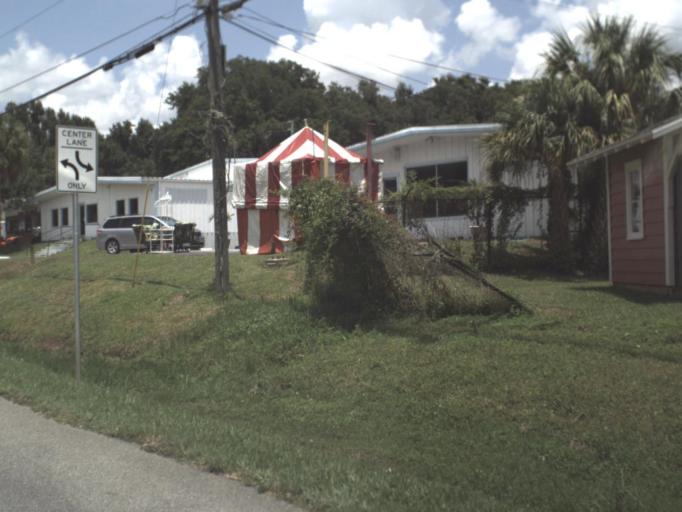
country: US
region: Florida
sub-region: Hernando County
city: North Brooksville
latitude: 28.5697
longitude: -82.3977
